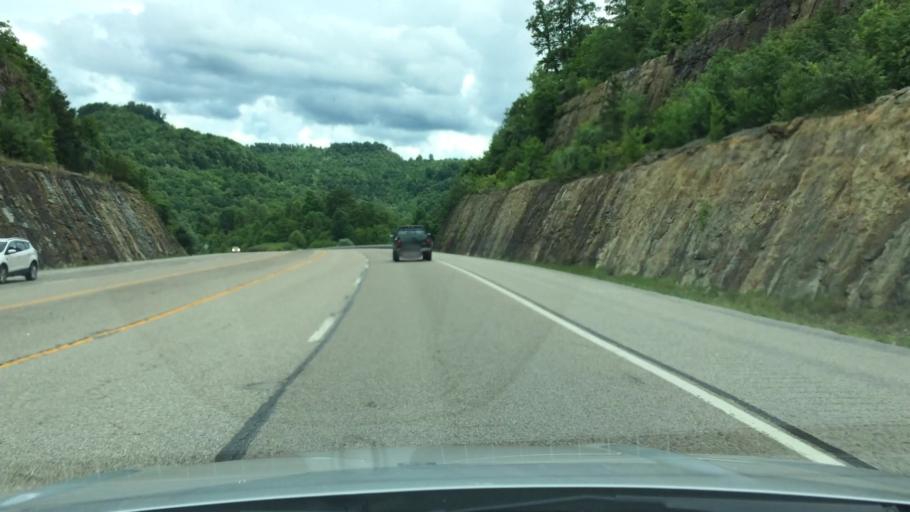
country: US
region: Kentucky
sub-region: Letcher County
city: Jenkins
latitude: 37.1953
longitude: -82.6244
